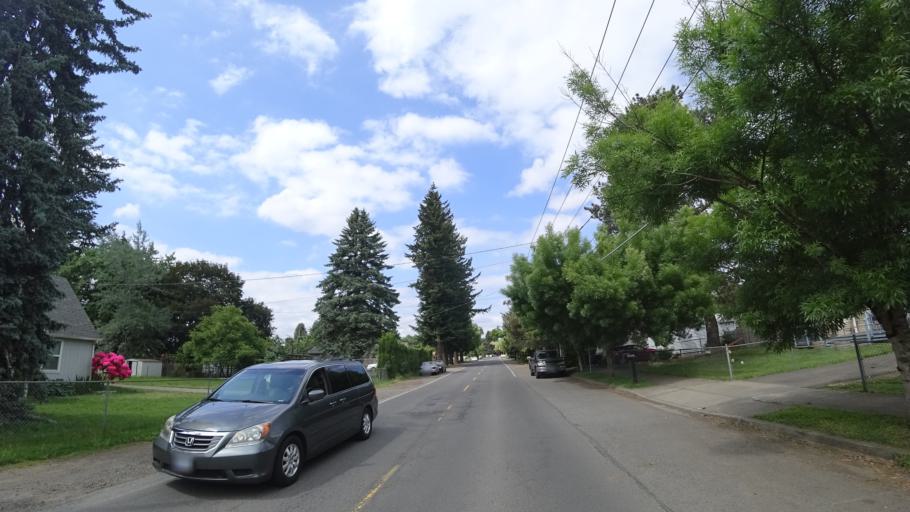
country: US
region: Oregon
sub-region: Multnomah County
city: Gresham
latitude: 45.5116
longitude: -122.4847
